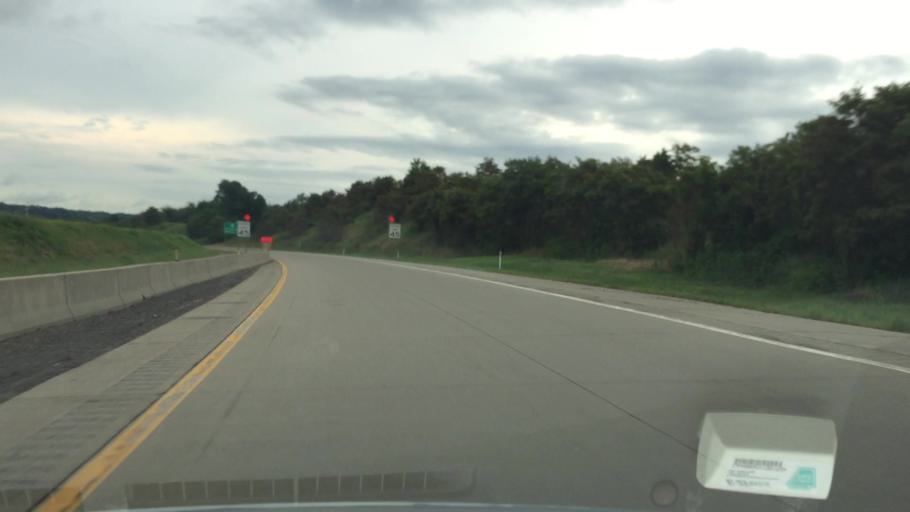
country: US
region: Pennsylvania
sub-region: Allegheny County
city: Imperial
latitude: 40.4365
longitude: -80.3178
